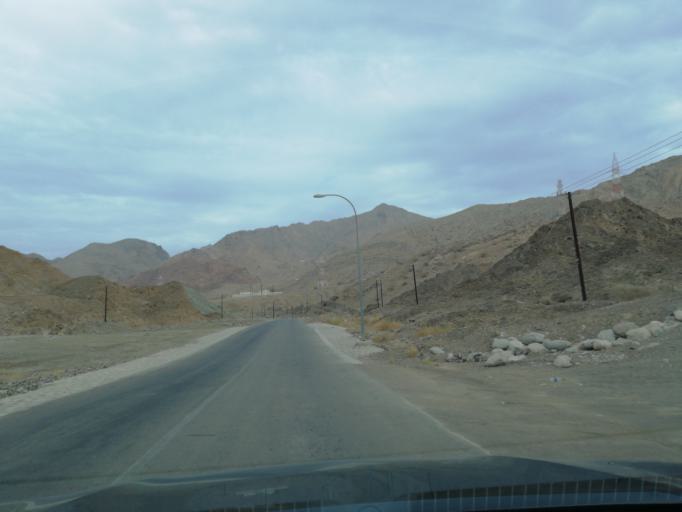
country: OM
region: Muhafazat Masqat
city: Bawshar
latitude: 23.4859
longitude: 58.3383
